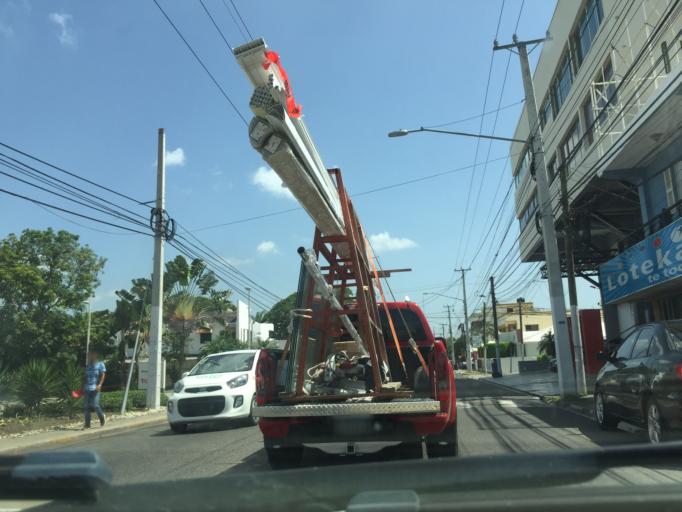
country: DO
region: Santiago
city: Santiago de los Caballeros
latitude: 19.4462
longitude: -70.6672
